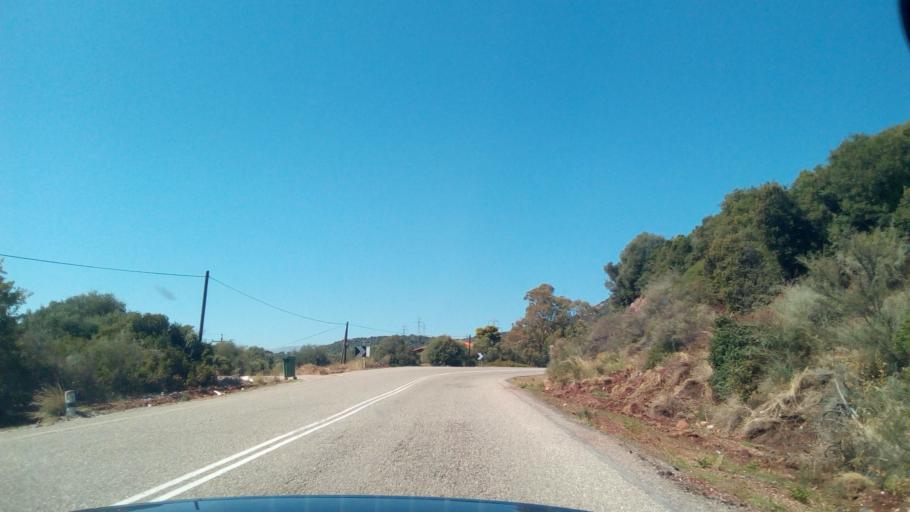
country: GR
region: West Greece
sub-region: Nomos Achaias
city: Kamarai
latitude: 38.4013
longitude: 21.9905
